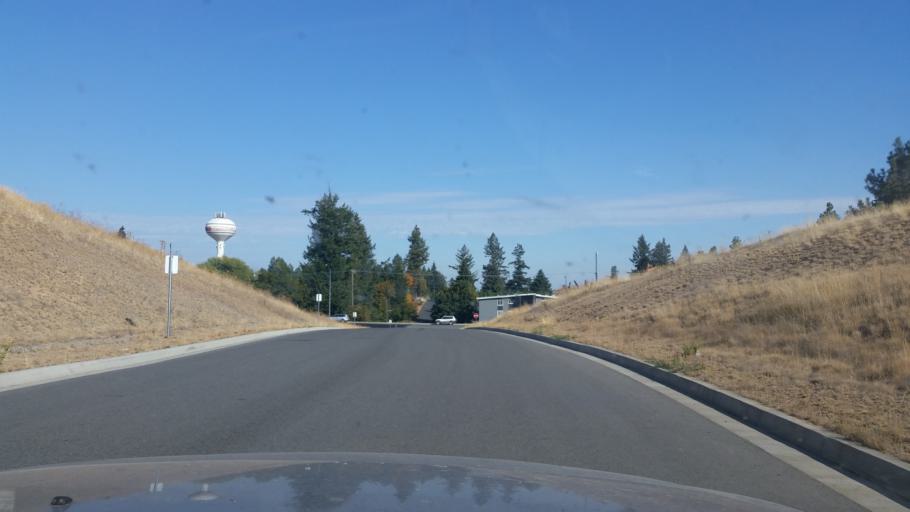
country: US
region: Washington
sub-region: Spokane County
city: Cheney
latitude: 47.4962
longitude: -117.5884
